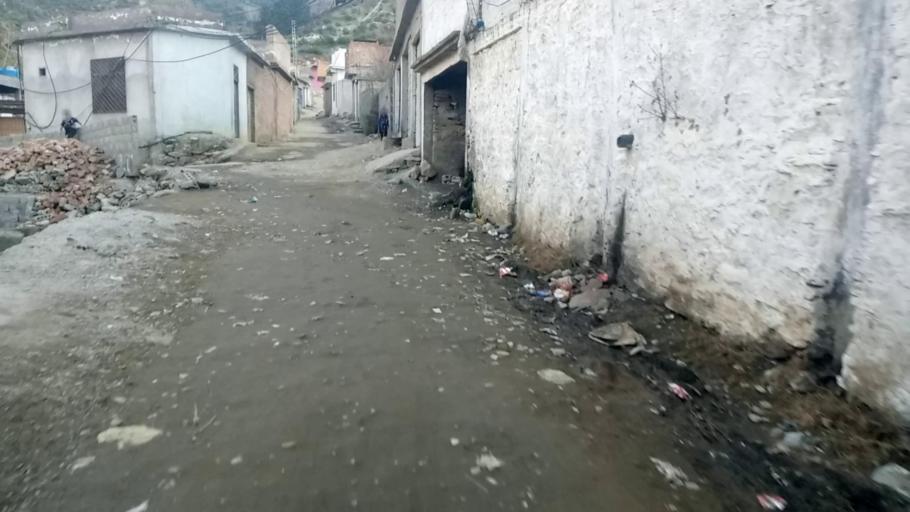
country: PK
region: Khyber Pakhtunkhwa
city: Saidu Sharif
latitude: 34.7379
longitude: 72.3521
